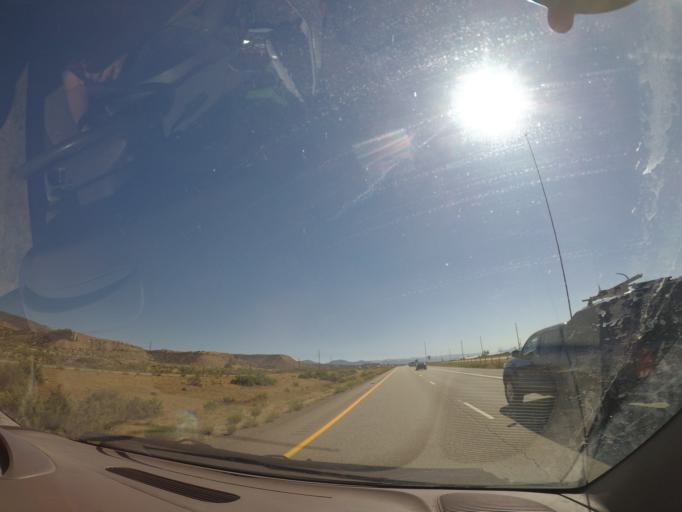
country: US
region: Colorado
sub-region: Garfield County
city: Rifle
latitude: 39.5172
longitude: -107.8562
